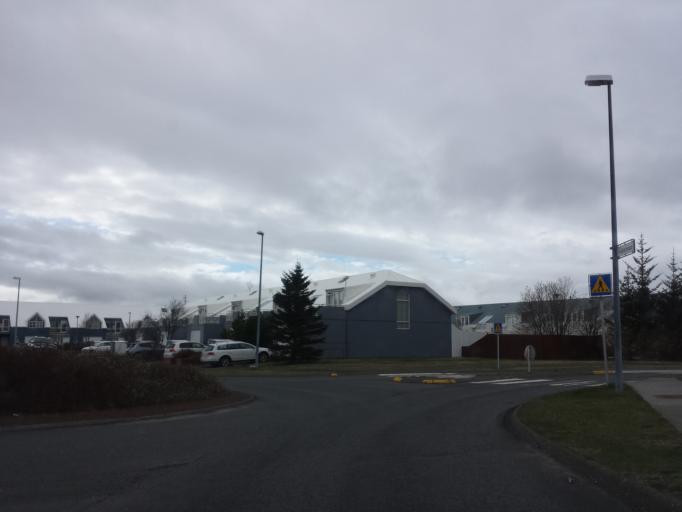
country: IS
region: Capital Region
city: Kopavogur
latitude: 64.0938
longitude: -21.8955
